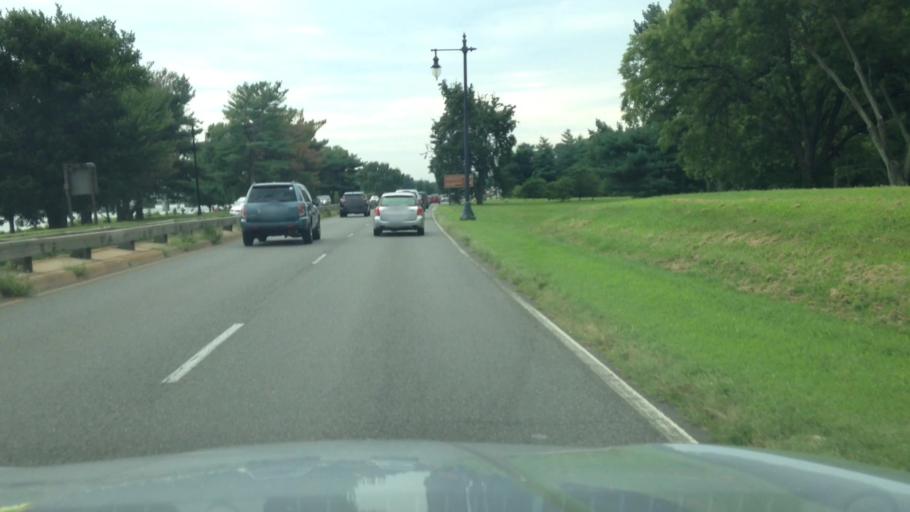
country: US
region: Washington, D.C.
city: Washington, D.C.
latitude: 38.8791
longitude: -77.0508
